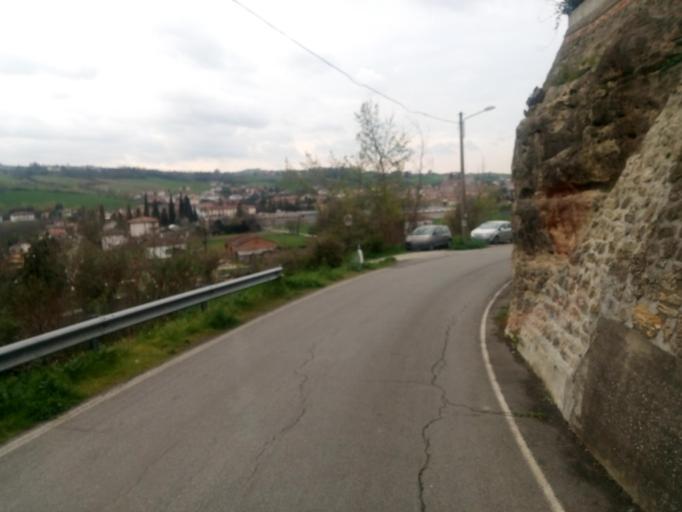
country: IT
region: Emilia-Romagna
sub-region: Forli-Cesena
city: Meldola
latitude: 44.1184
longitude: 12.0686
